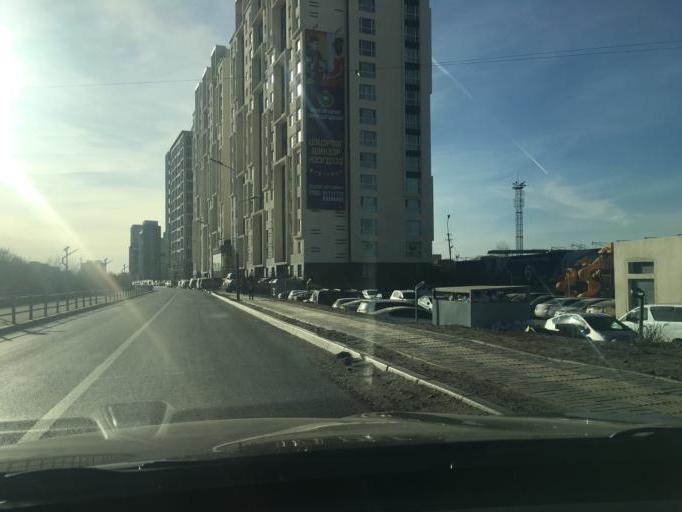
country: MN
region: Ulaanbaatar
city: Ulaanbaatar
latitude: 47.9069
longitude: 106.9110
